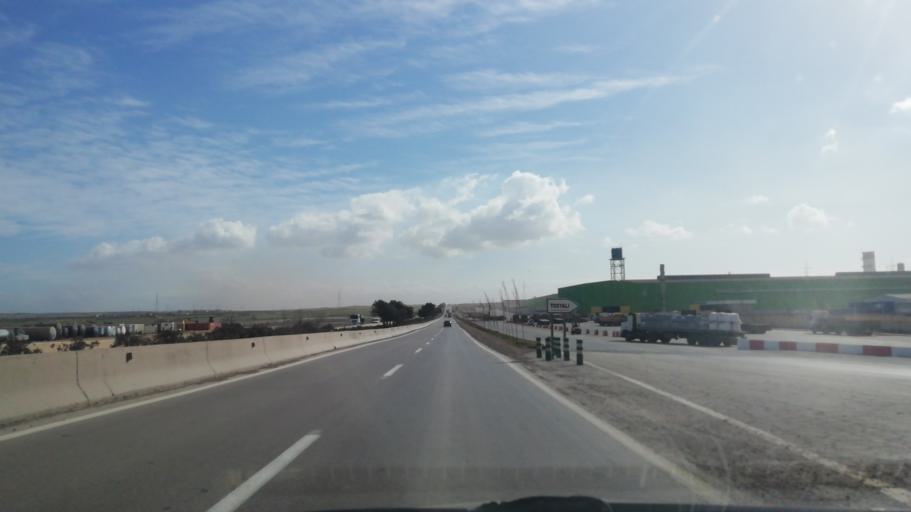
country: DZ
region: Oran
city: Ain el Bya
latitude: 35.7771
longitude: -0.2607
